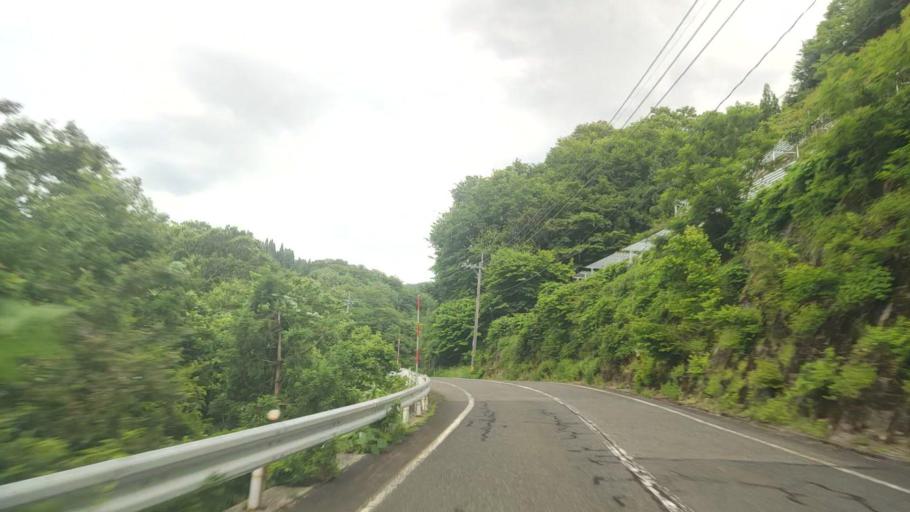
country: JP
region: Tottori
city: Kurayoshi
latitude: 35.3185
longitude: 134.0096
